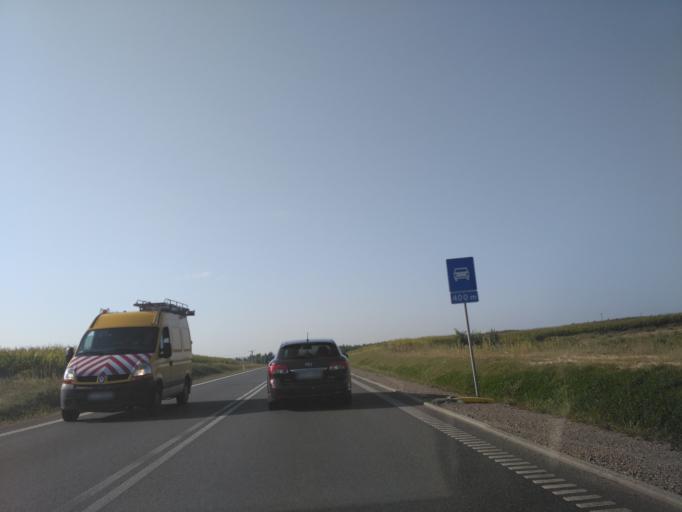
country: PL
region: Subcarpathian Voivodeship
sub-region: Powiat rzeszowski
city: Sokolow Malopolski
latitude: 50.2499
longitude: 22.1369
